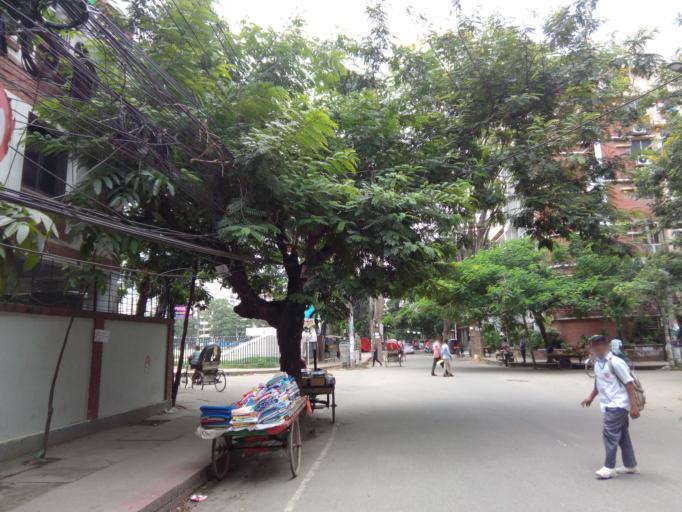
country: BD
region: Dhaka
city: Azimpur
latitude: 23.7486
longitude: 90.3725
